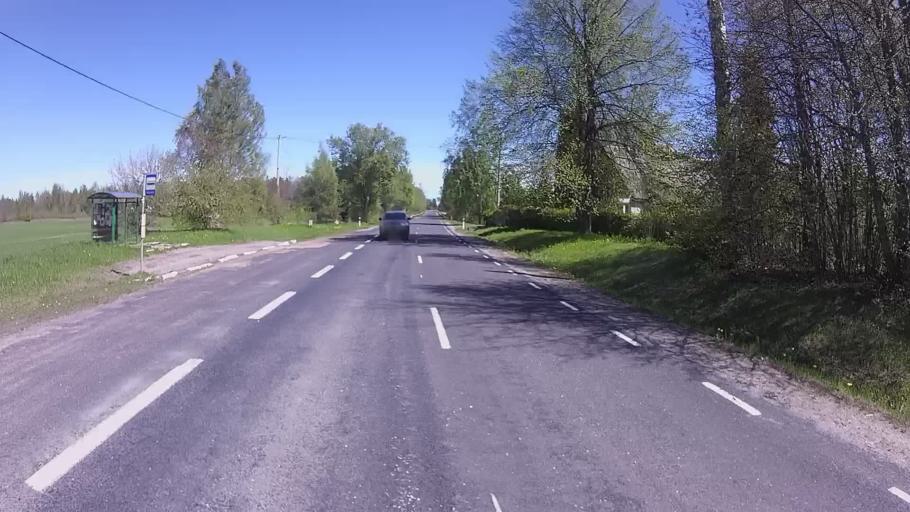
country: EE
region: Polvamaa
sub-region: Raepina vald
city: Rapina
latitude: 58.0270
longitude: 27.3802
